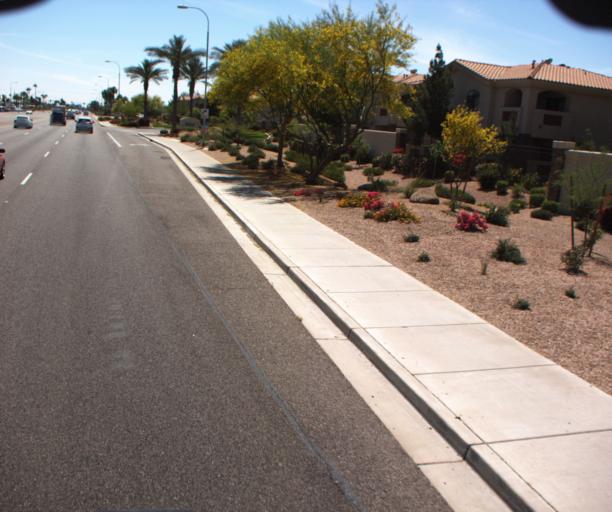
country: US
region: Arizona
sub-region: Maricopa County
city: San Carlos
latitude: 33.3314
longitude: -111.8418
